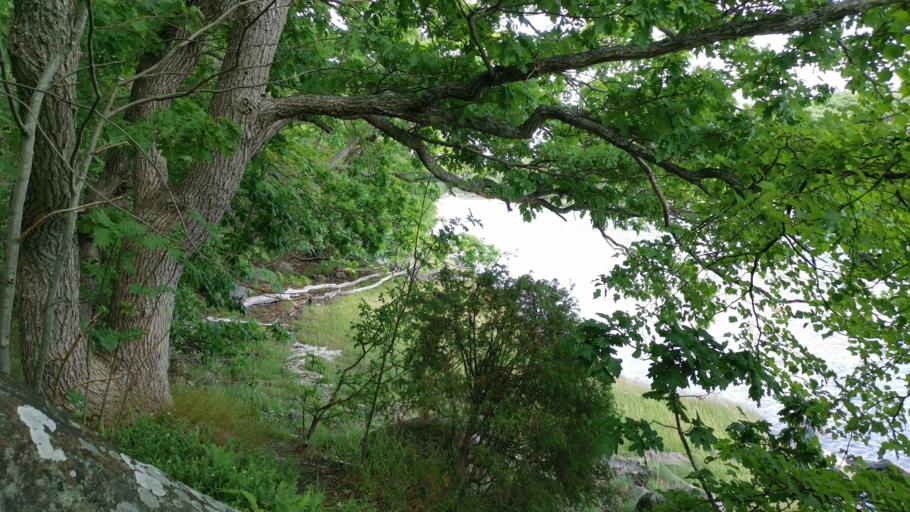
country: SE
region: Vaestra Goetaland
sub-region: Lysekils Kommun
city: Lysekil
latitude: 58.2407
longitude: 11.4897
